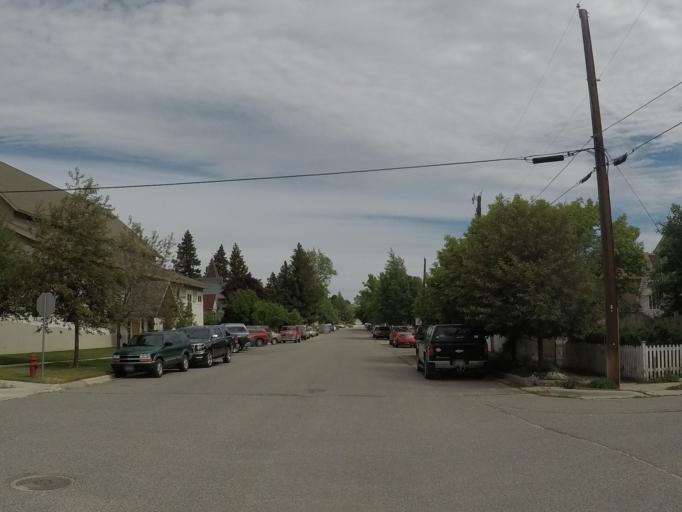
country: US
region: Montana
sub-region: Carbon County
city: Red Lodge
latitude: 45.1868
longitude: -109.2498
